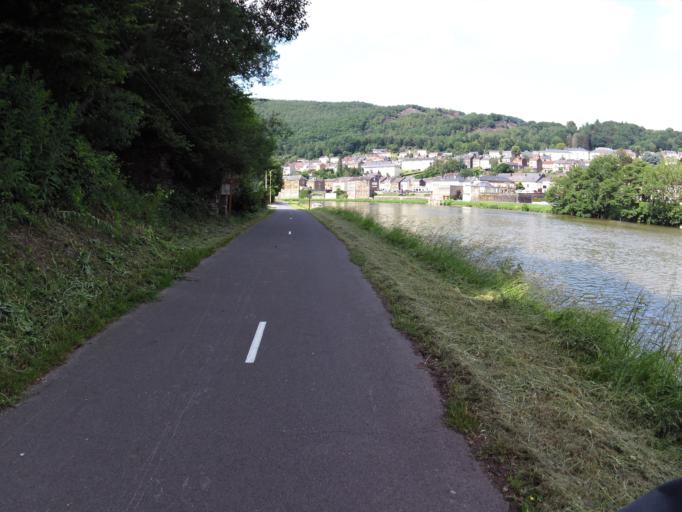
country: FR
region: Champagne-Ardenne
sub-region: Departement des Ardennes
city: Montherme
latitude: 49.8833
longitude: 4.7370
